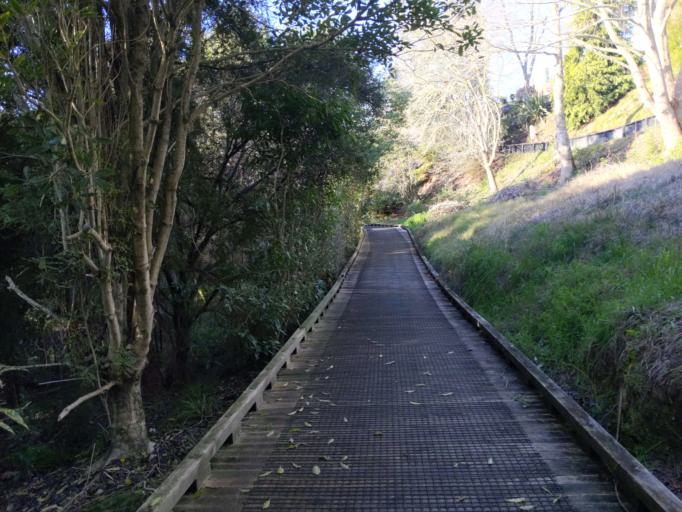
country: NZ
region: Waikato
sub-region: Hamilton City
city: Hamilton
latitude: -37.7416
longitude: 175.2747
